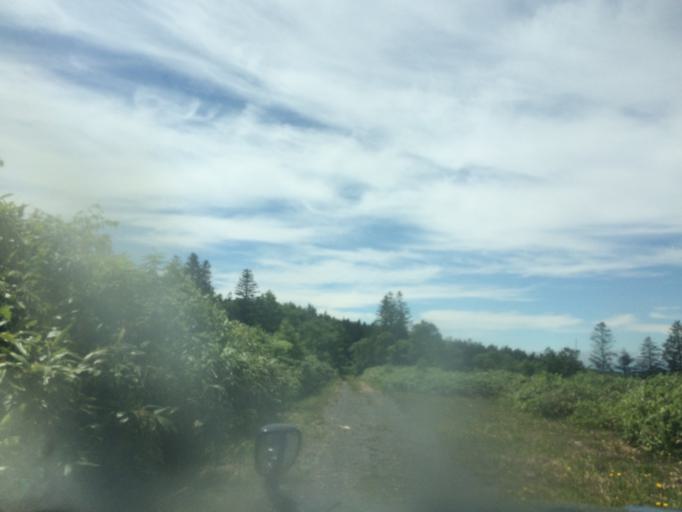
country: JP
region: Hokkaido
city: Niseko Town
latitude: 42.8607
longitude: 140.8212
